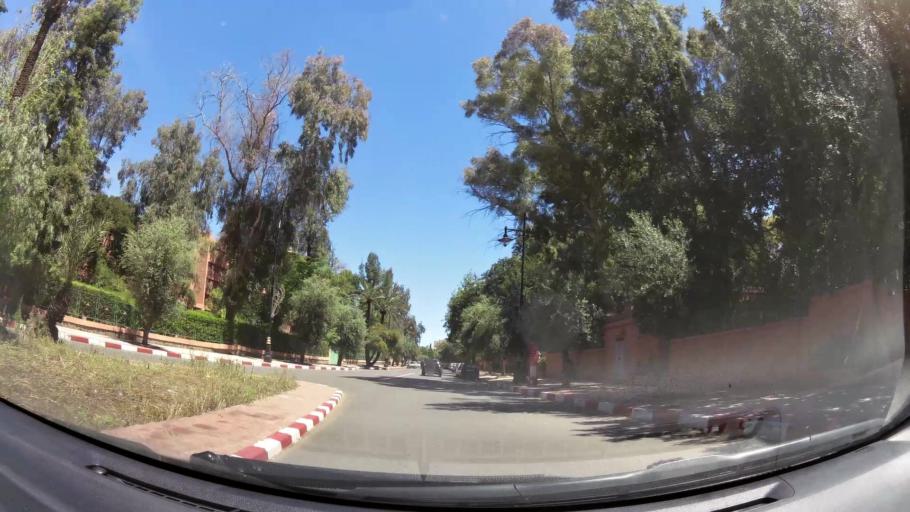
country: MA
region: Marrakech-Tensift-Al Haouz
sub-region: Marrakech
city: Marrakesh
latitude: 31.6217
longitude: -8.0063
